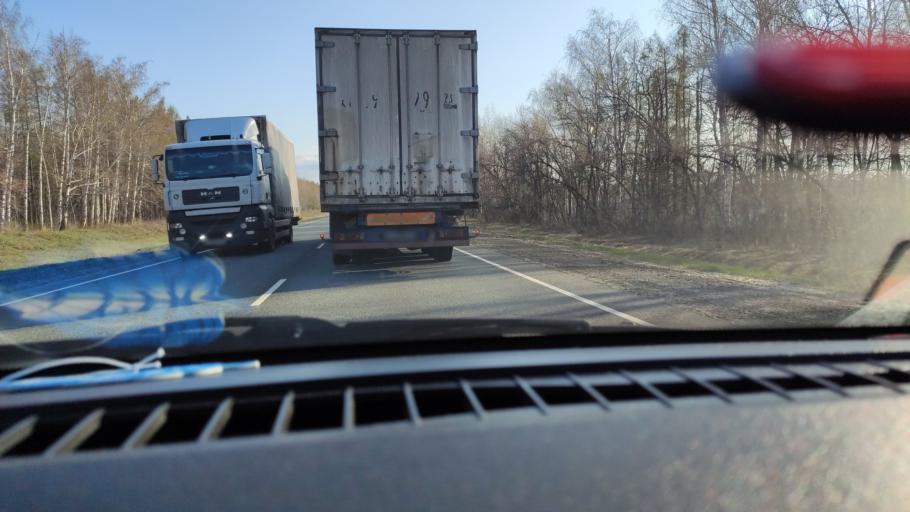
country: RU
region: Saratov
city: Khvalynsk
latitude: 52.5711
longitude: 48.1027
